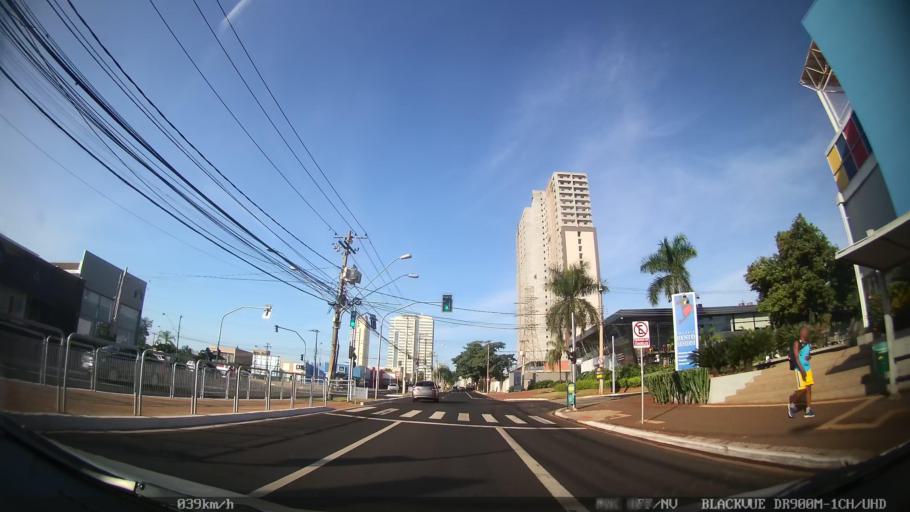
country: BR
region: Sao Paulo
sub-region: Ribeirao Preto
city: Ribeirao Preto
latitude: -21.1953
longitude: -47.8075
